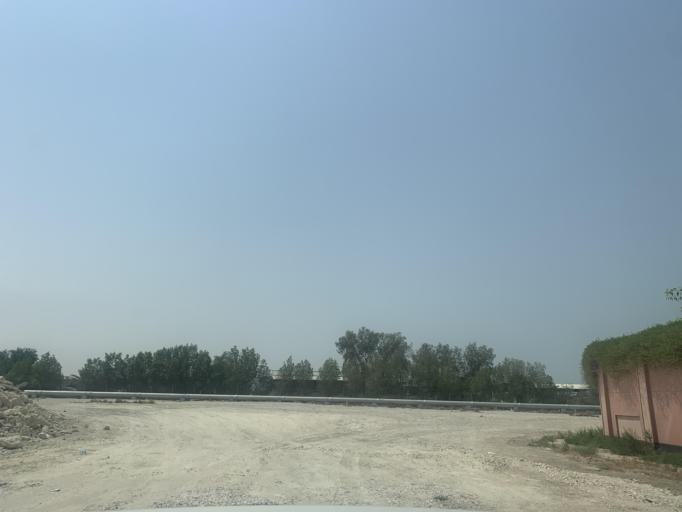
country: BH
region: Central Governorate
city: Madinat Hamad
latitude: 26.1442
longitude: 50.4787
